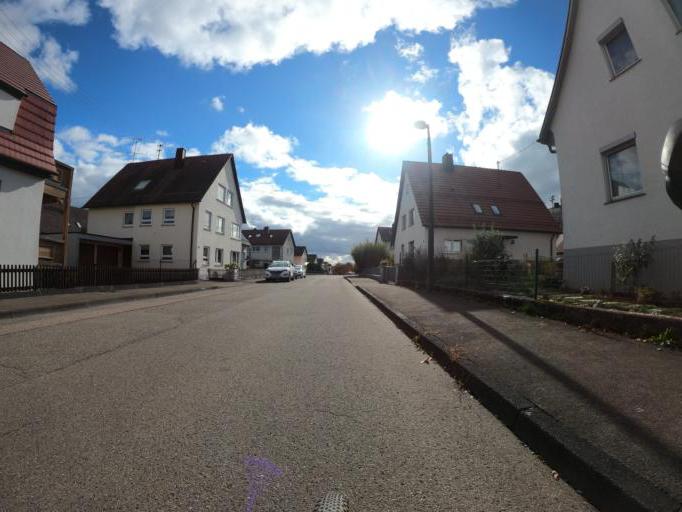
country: DE
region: Baden-Wuerttemberg
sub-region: Regierungsbezirk Stuttgart
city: Magstadt
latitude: 48.7222
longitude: 8.9619
